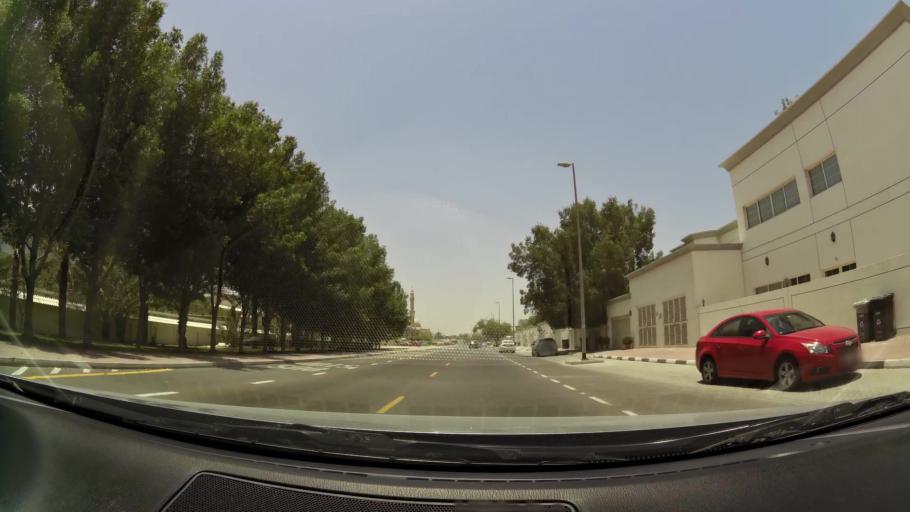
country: AE
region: Dubai
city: Dubai
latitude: 25.1752
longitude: 55.2241
